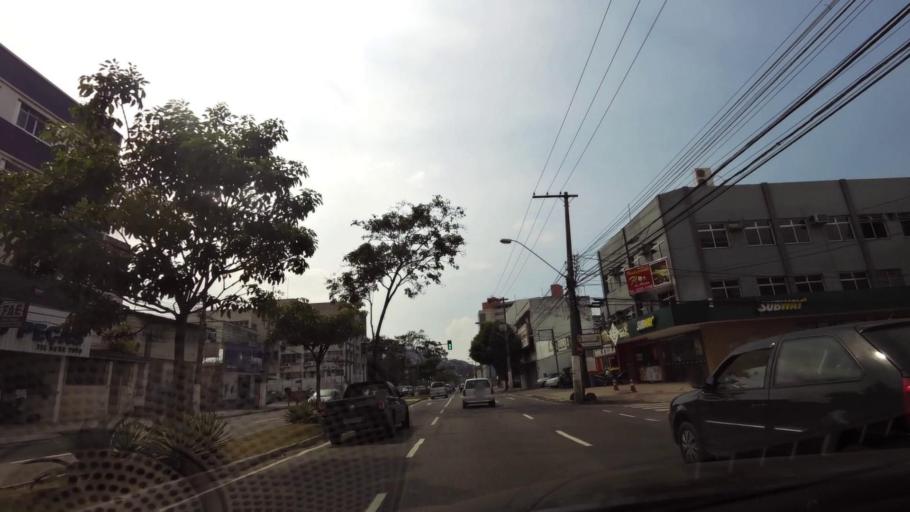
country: BR
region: Espirito Santo
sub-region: Vitoria
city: Vitoria
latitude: -20.3112
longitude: -40.3169
